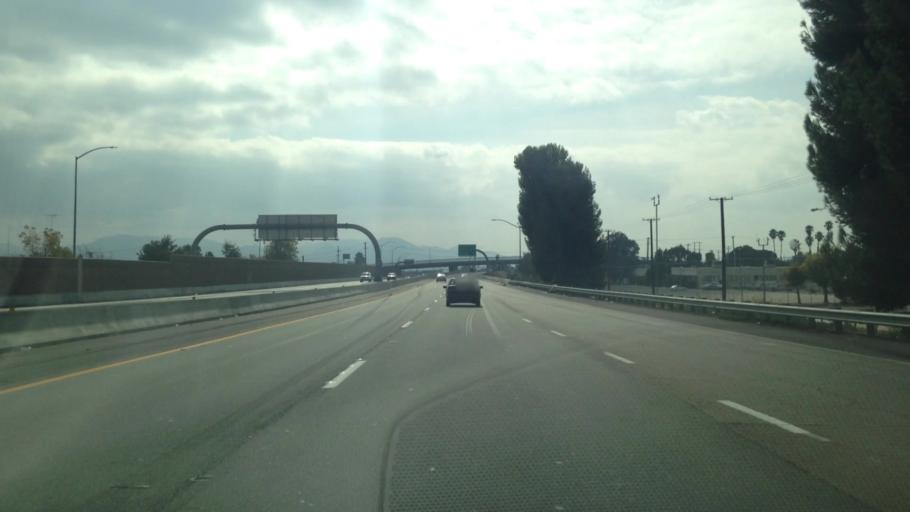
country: US
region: California
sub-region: San Bernardino County
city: San Bernardino
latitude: 34.1338
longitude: -117.3029
